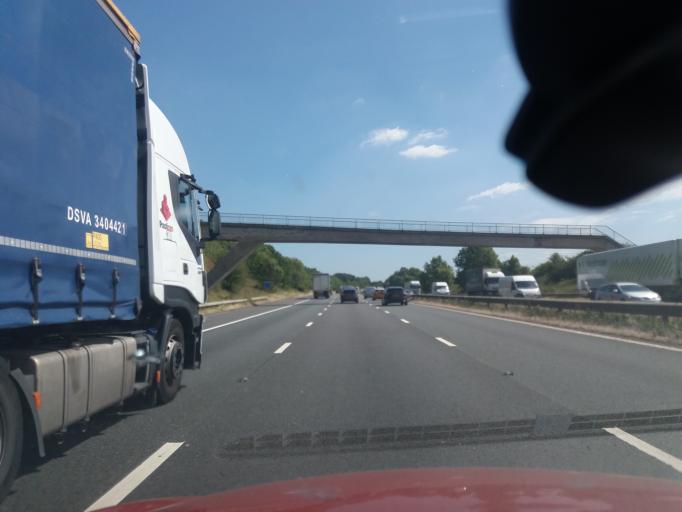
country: GB
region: England
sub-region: Lancashire
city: Chorley
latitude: 53.6467
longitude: -2.6050
